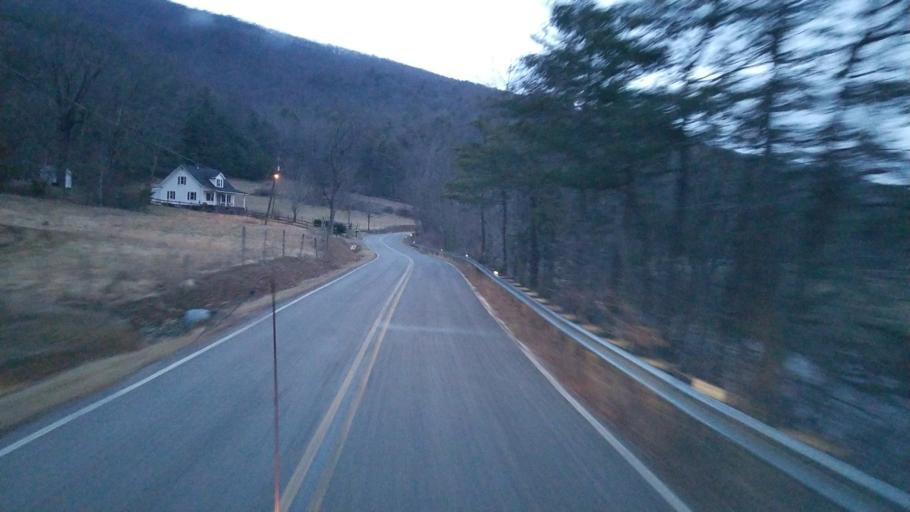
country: US
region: Virginia
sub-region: Pulaski County
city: Pulaski
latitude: 37.1352
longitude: -80.8522
